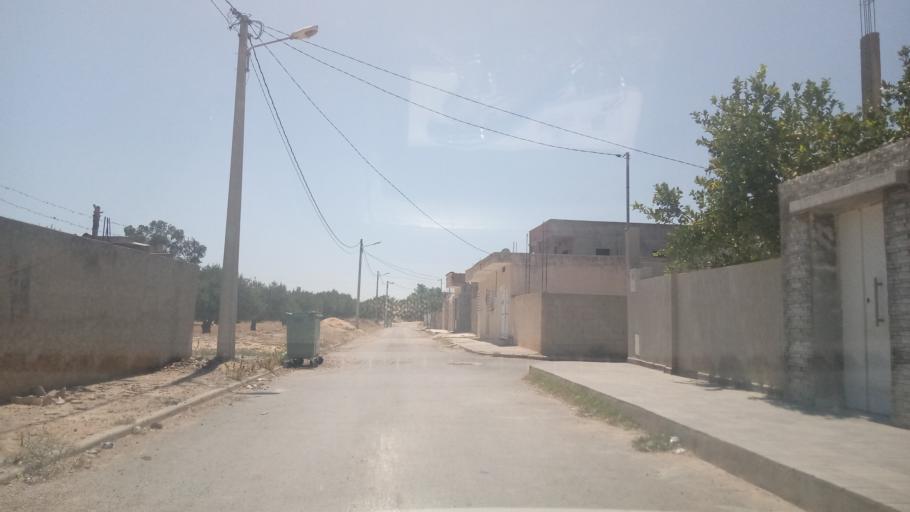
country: TN
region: Al Qayrawan
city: Sbikha
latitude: 36.1177
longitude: 10.0893
